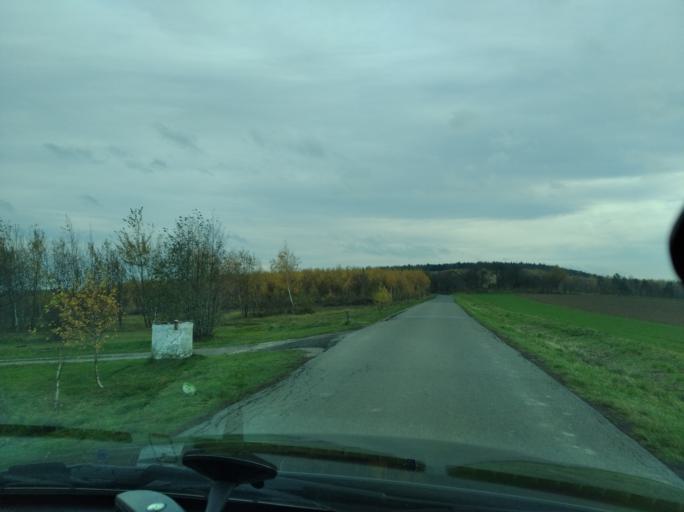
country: PL
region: Subcarpathian Voivodeship
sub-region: Powiat strzyzowski
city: Strzyzow
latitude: 49.9168
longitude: 21.7650
